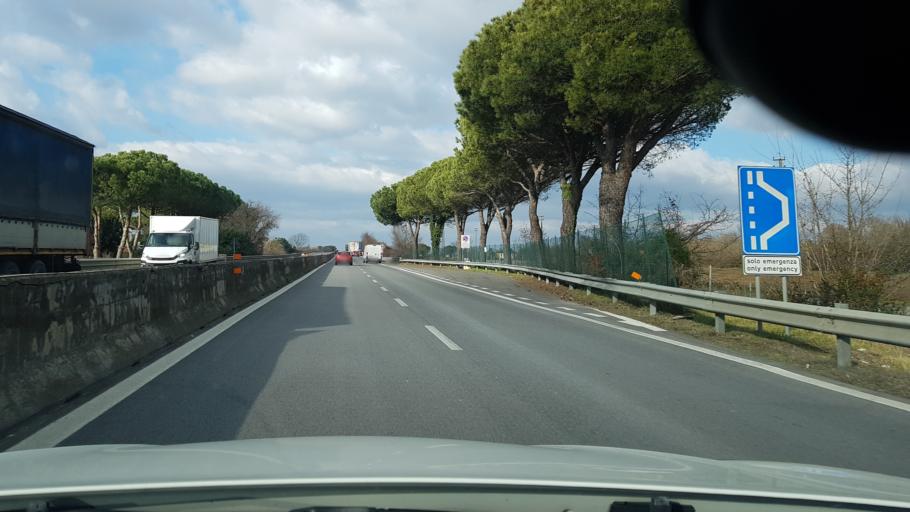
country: IT
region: Tuscany
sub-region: Province of Arezzo
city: Terontola
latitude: 43.1873
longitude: 12.0292
